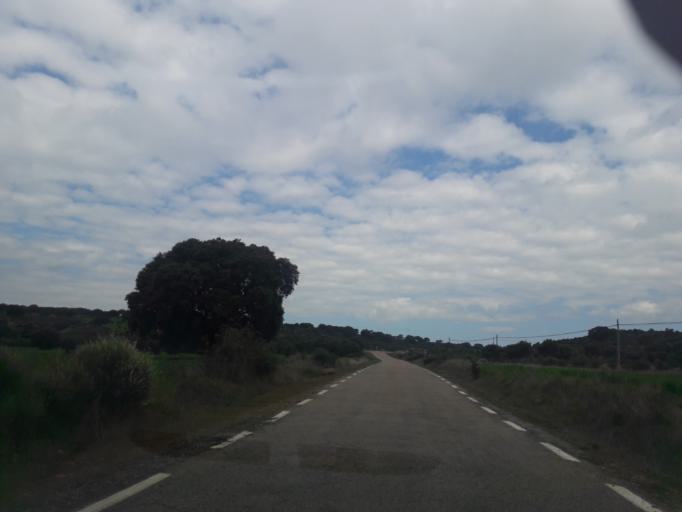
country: ES
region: Castille and Leon
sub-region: Provincia de Salamanca
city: Serradilla del Arroyo
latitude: 40.5236
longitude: -6.3801
